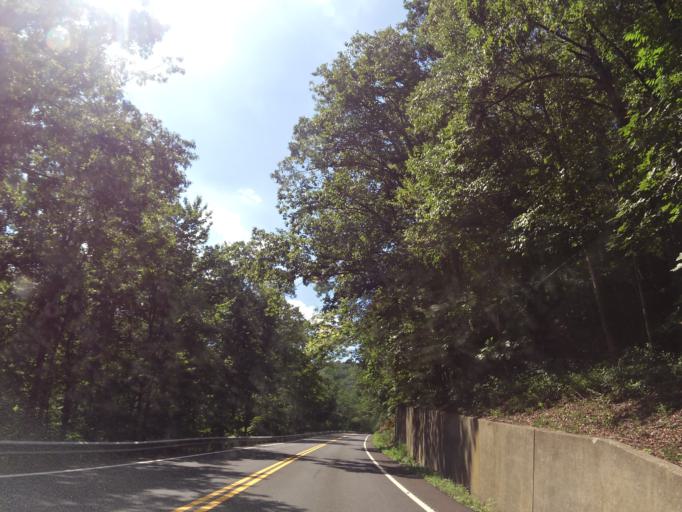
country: US
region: Tennessee
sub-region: Roane County
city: Rockwood
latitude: 35.8787
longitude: -84.8179
